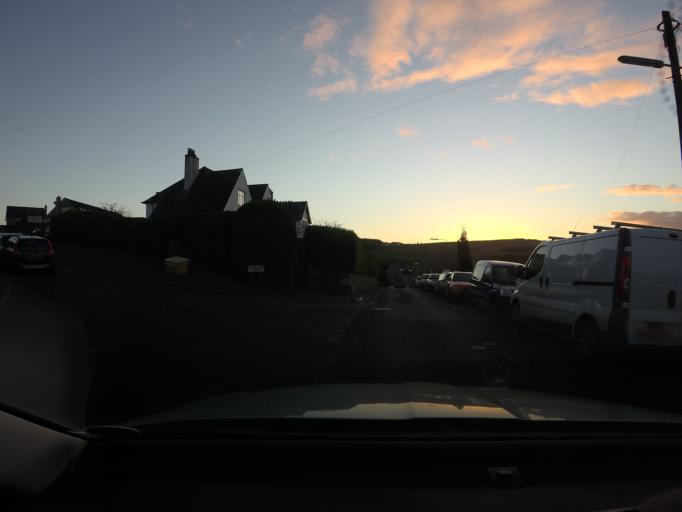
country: GB
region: Scotland
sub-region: Dundee City
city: Dundee
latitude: 56.4236
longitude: -2.9848
